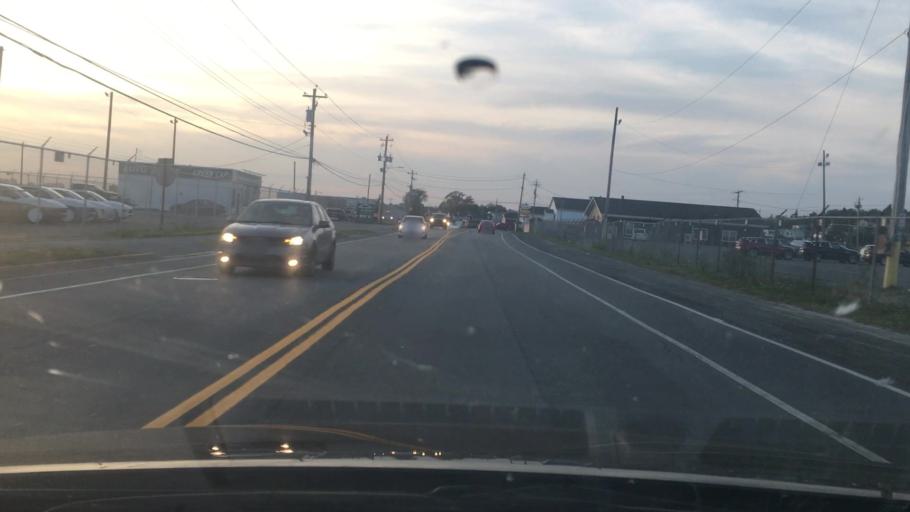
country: CA
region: Nova Scotia
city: Cole Harbour
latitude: 44.6222
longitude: -63.5086
